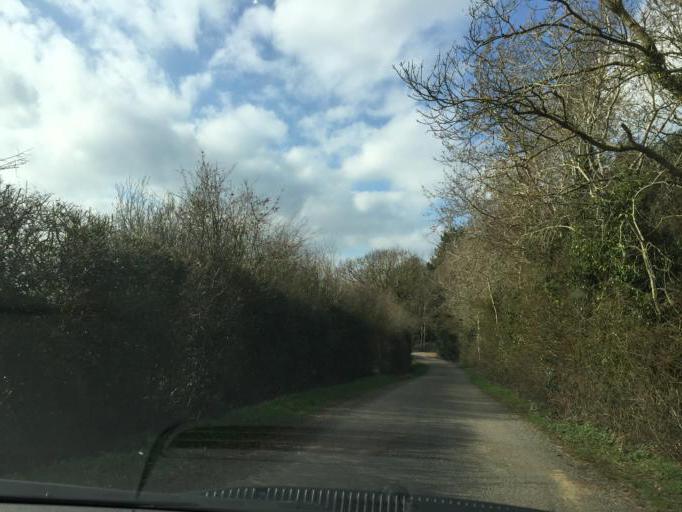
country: GB
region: England
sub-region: Coventry
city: Keresley
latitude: 52.4497
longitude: -1.5866
